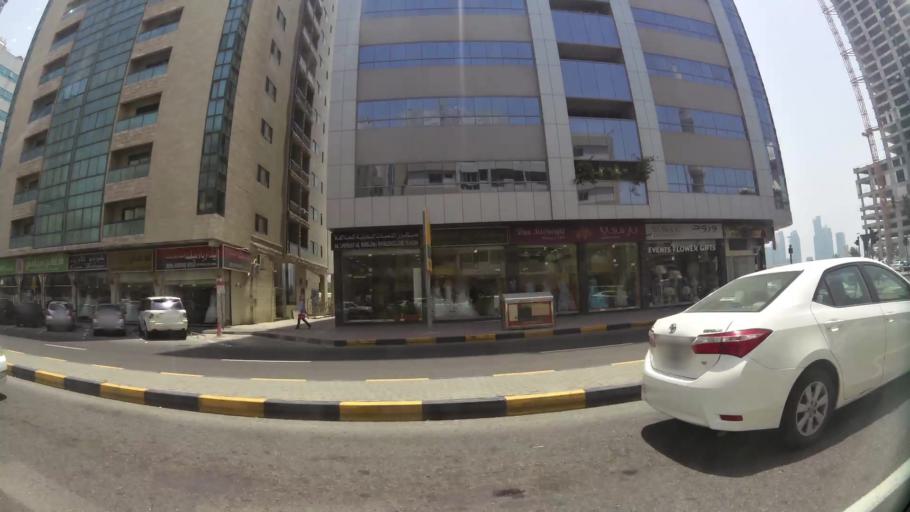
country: AE
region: Ash Shariqah
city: Sharjah
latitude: 25.3310
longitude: 55.3918
